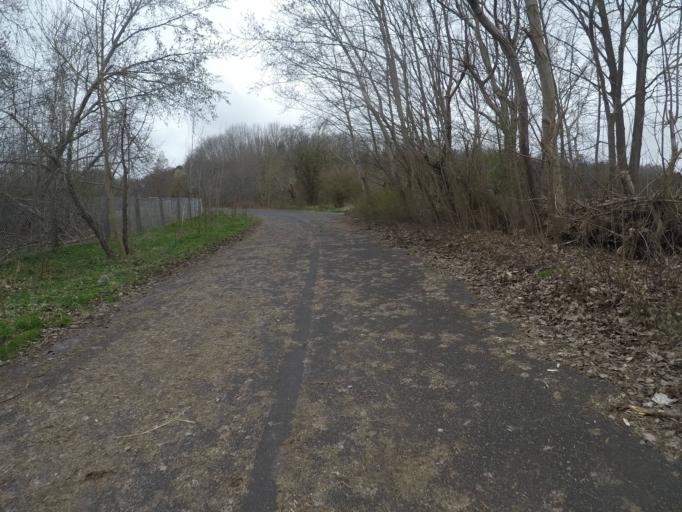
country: DE
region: Lower Saxony
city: Nordholz
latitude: 53.8163
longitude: 8.6550
